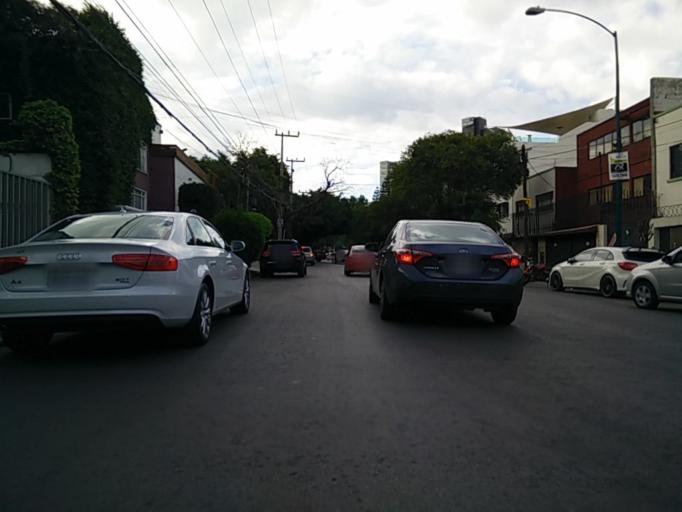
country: MX
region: Mexico City
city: Miguel Hidalgo
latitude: 19.4323
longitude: -99.1793
